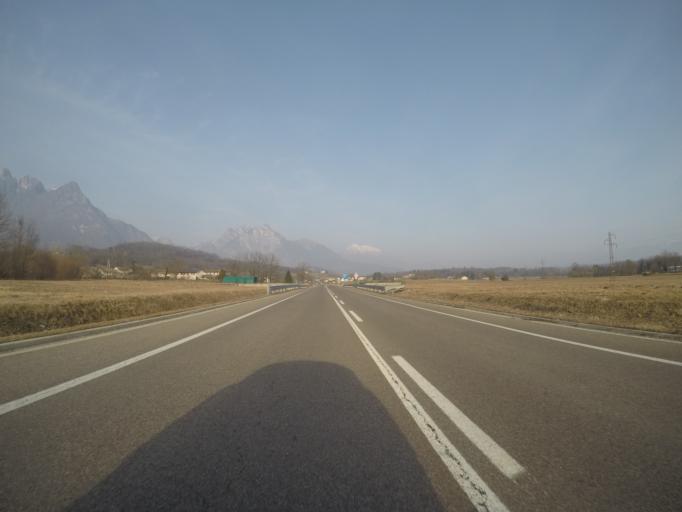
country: IT
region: Veneto
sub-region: Provincia di Belluno
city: Sospirolo
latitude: 46.1384
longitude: 12.0883
